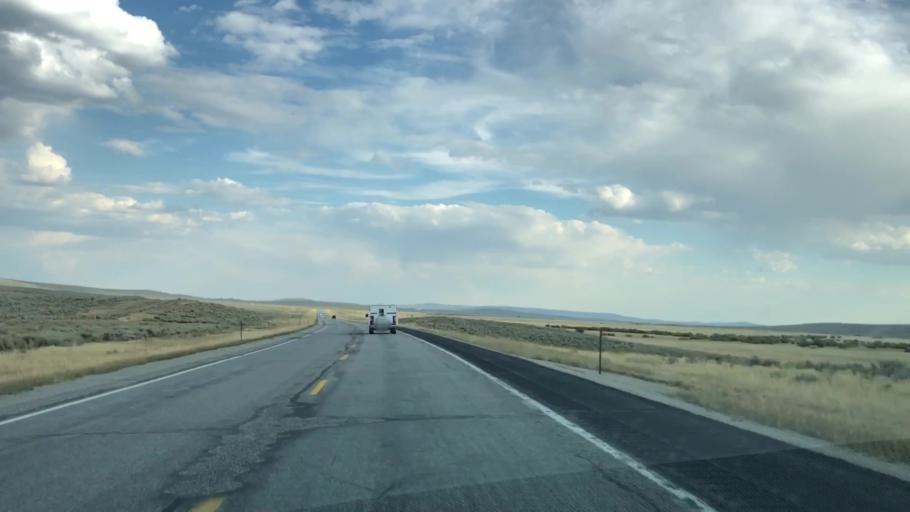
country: US
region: Wyoming
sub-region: Sublette County
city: Pinedale
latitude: 43.0469
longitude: -110.1479
